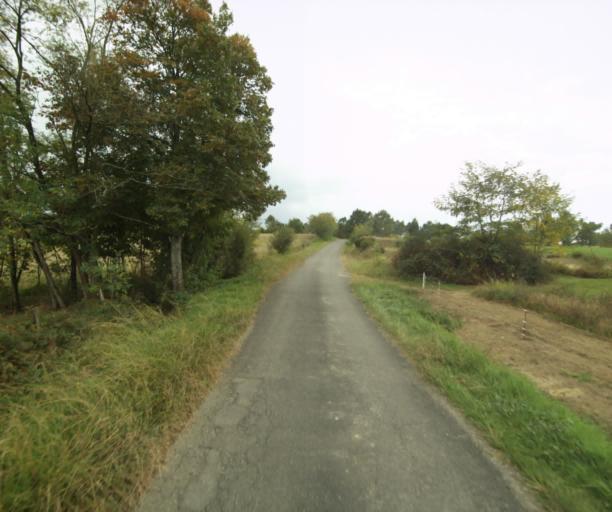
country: FR
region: Midi-Pyrenees
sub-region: Departement du Gers
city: Eauze
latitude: 43.9021
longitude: 0.1191
